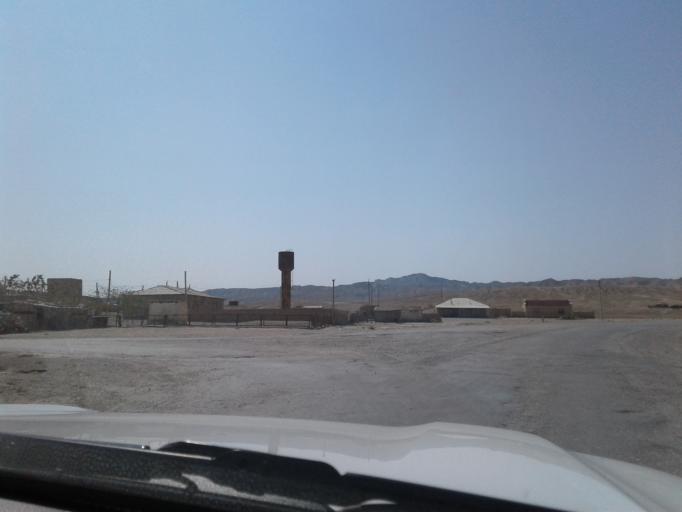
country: TM
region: Balkan
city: Gazanjyk
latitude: 39.1489
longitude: 55.3084
